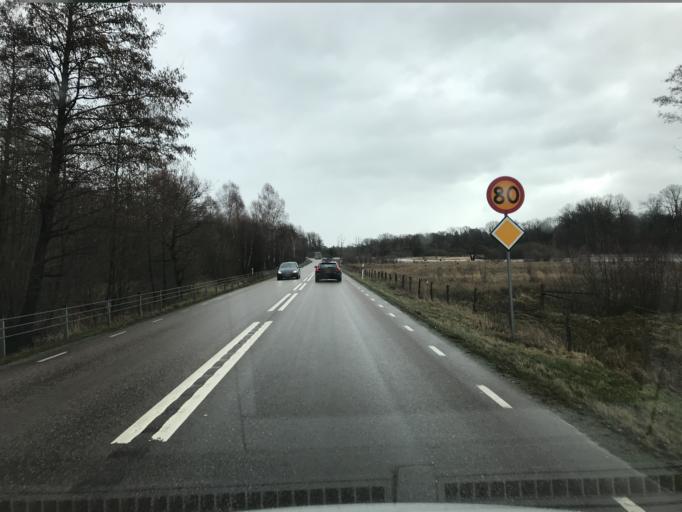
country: SE
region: Skane
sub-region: Klippans Kommun
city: Ljungbyhed
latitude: 56.0903
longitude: 13.2239
